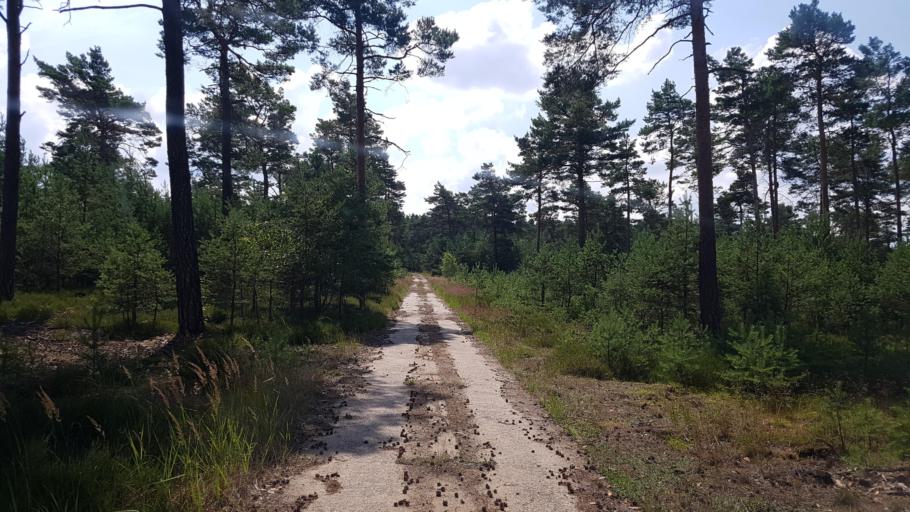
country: DE
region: Brandenburg
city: Crinitz
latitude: 51.7034
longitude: 13.7411
